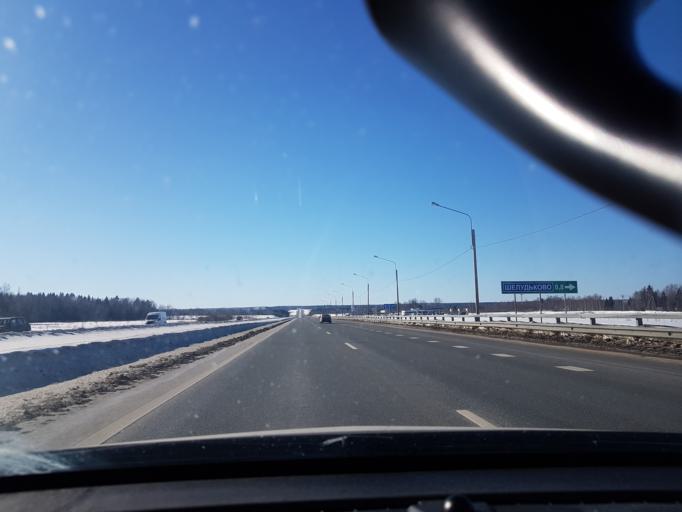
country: RU
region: Moskovskaya
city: Sychevo
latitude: 55.9891
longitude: 36.2763
